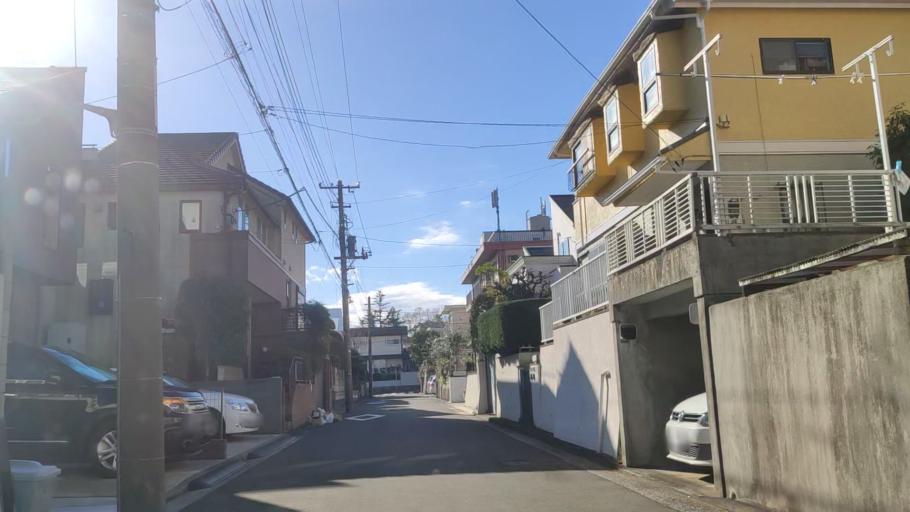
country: JP
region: Kanagawa
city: Yokohama
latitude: 35.4247
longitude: 139.6538
